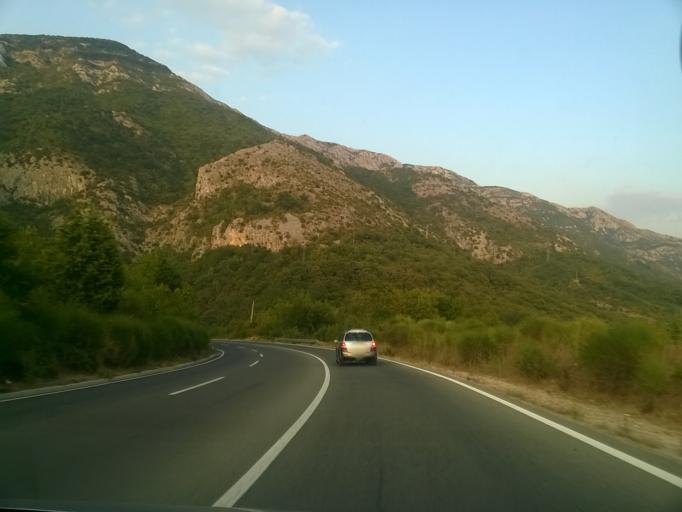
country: ME
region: Bar
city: Sutomore
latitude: 42.1721
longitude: 19.0034
